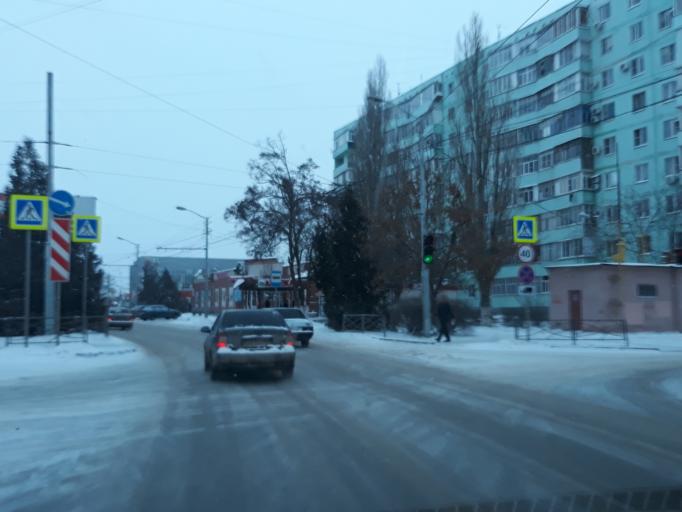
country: RU
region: Rostov
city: Taganrog
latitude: 47.2674
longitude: 38.9235
